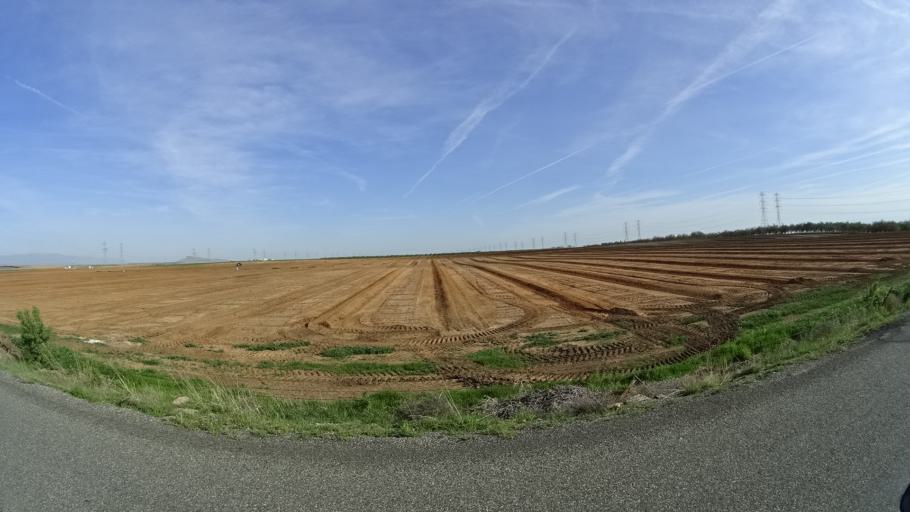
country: US
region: California
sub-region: Glenn County
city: Orland
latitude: 39.6682
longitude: -122.2682
